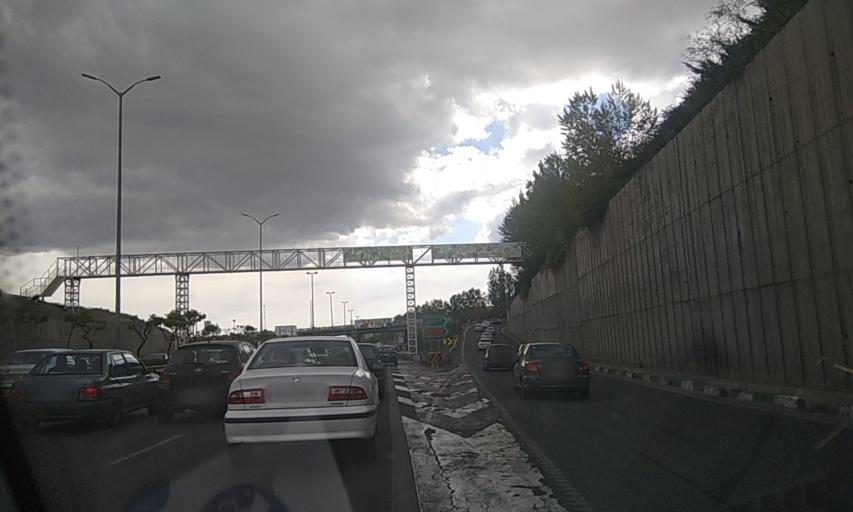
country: IR
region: Tehran
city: Tajrish
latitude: 35.7709
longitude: 51.3399
